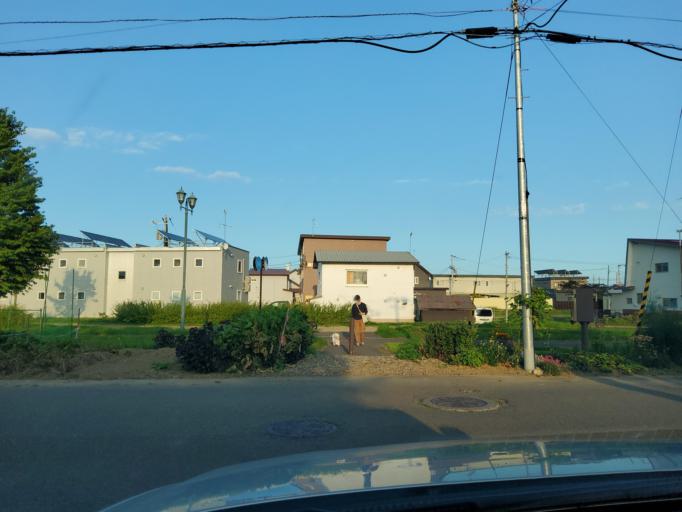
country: JP
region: Hokkaido
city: Obihiro
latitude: 42.9323
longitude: 143.1897
